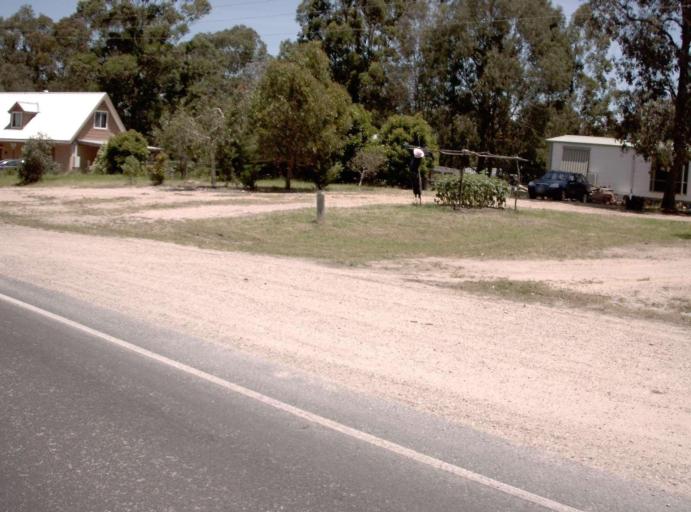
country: AU
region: Victoria
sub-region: East Gippsland
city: Lakes Entrance
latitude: -37.6943
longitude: 147.8360
